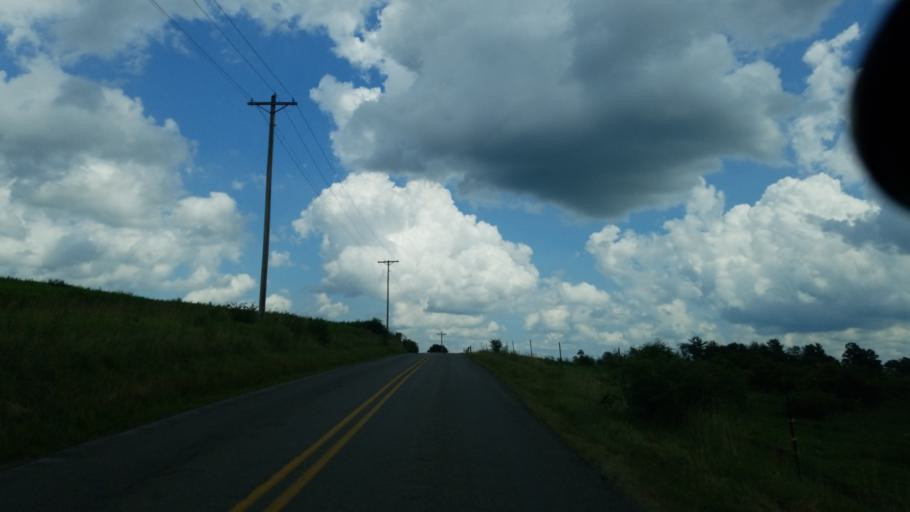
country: US
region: Pennsylvania
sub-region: Jefferson County
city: Brookville
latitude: 41.2328
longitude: -79.0756
